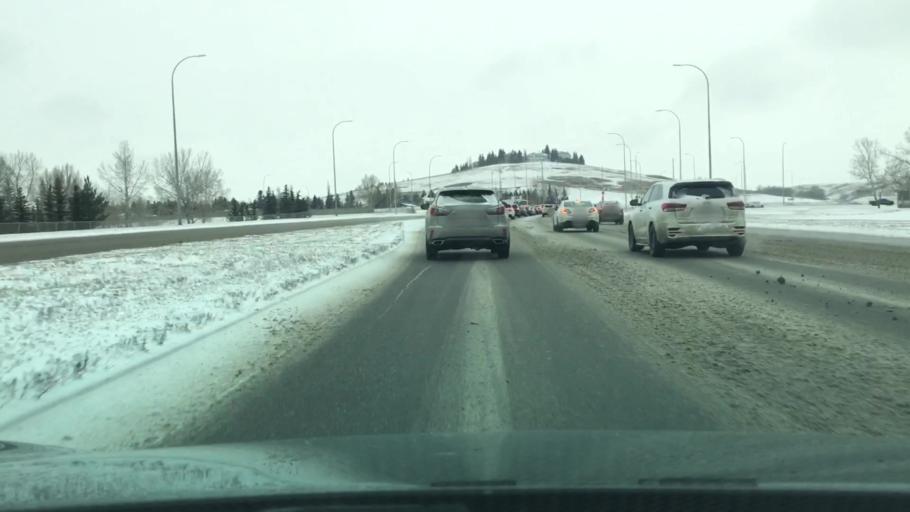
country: CA
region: Alberta
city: Calgary
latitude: 51.1068
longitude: -114.1401
